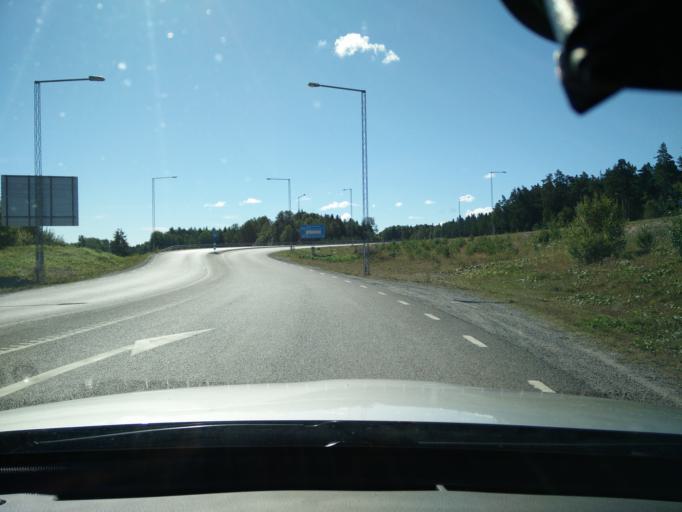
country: SE
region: Stockholm
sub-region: Vallentuna Kommun
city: Vallentuna
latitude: 59.4883
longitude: 18.1106
